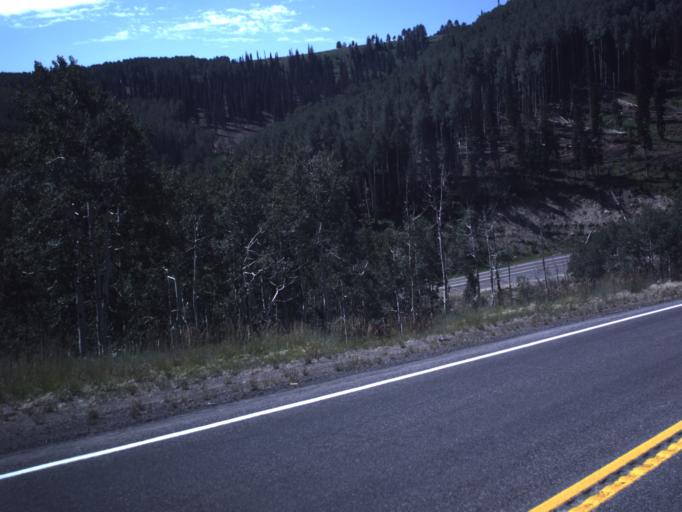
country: US
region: Utah
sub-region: Sanpete County
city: Fairview
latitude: 39.6800
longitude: -111.2134
